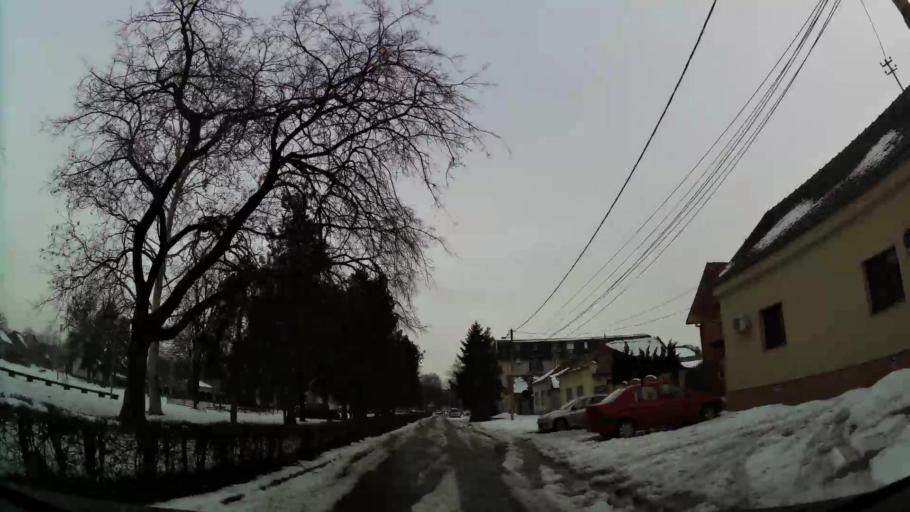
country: RS
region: Central Serbia
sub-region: Belgrade
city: Zemun
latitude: 44.8555
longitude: 20.3812
